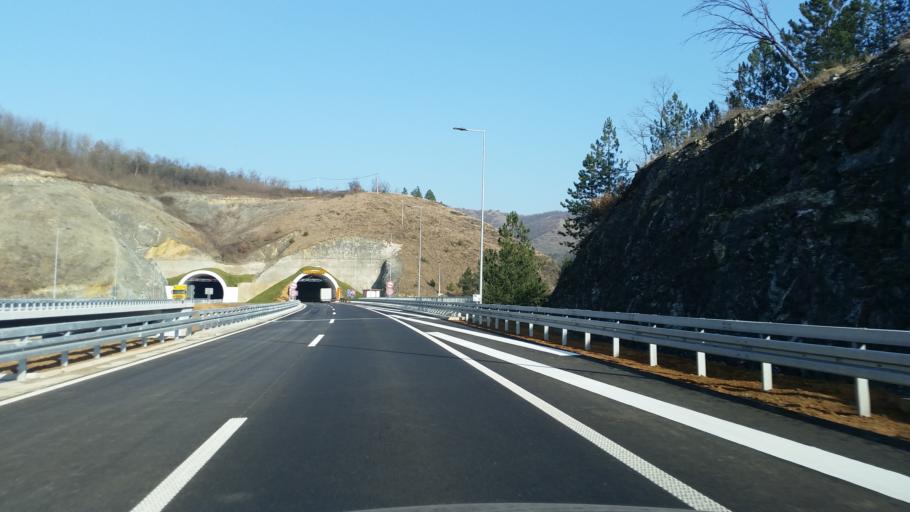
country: RS
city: Prislonica
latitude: 43.9759
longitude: 20.3997
